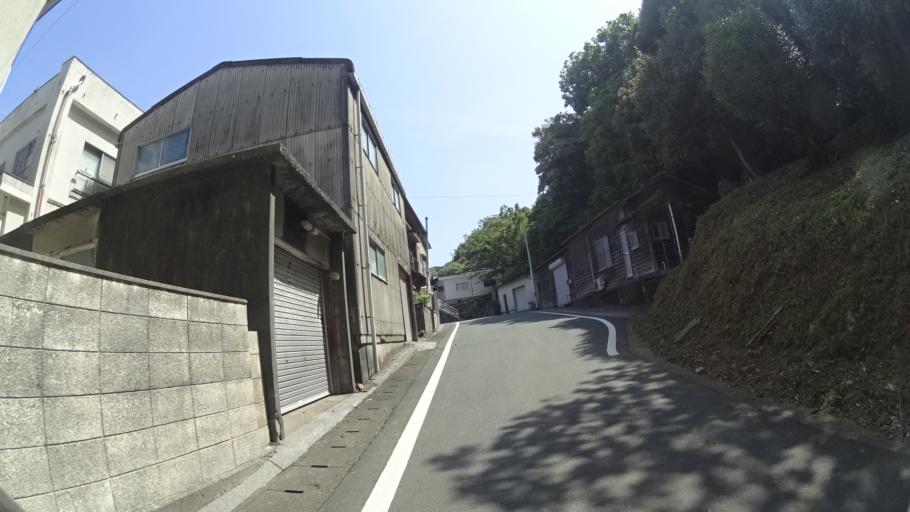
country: JP
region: Ehime
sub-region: Nishiuwa-gun
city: Ikata-cho
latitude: 33.3722
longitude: 132.0532
